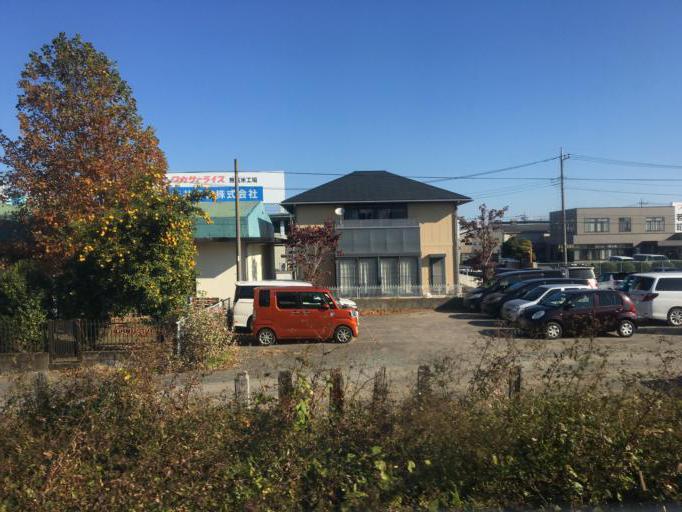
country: JP
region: Gunma
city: Maebashi-shi
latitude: 36.3682
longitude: 139.1139
